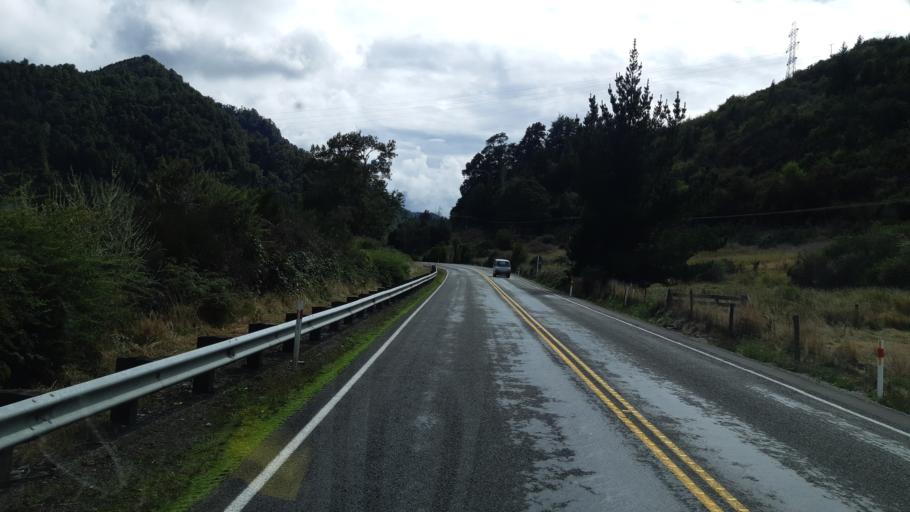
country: NZ
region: West Coast
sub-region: Buller District
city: Westport
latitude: -41.7945
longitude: 172.3649
